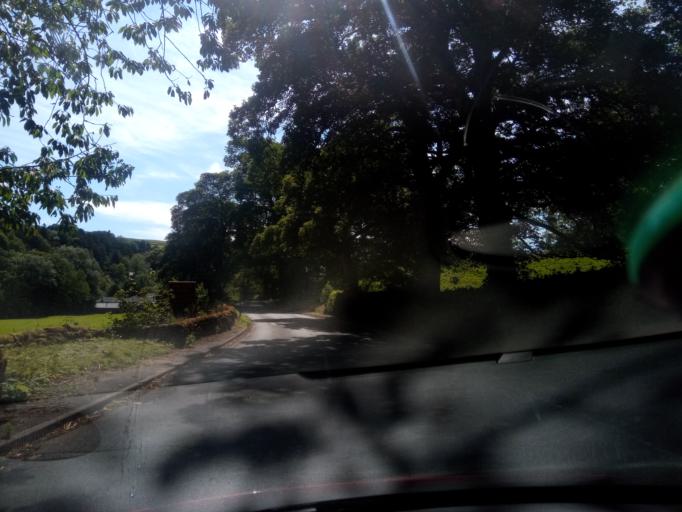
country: GB
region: England
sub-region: Northumberland
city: Bardon Mill
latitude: 54.9102
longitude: -2.3437
